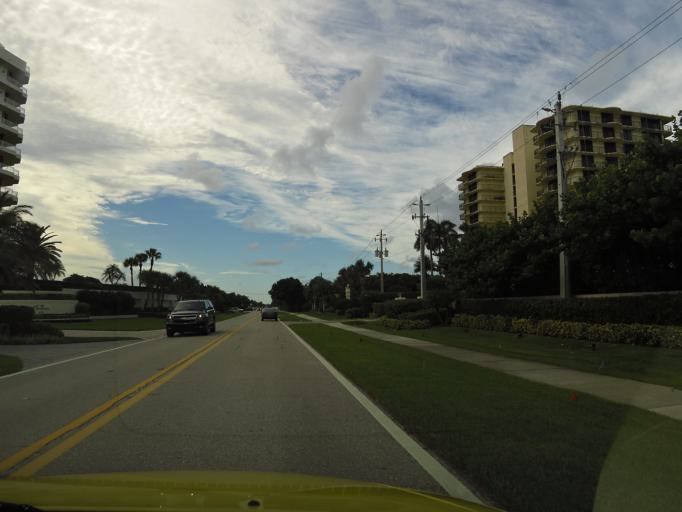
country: US
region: Florida
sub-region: Palm Beach County
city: Jupiter
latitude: 26.9549
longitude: -80.0767
